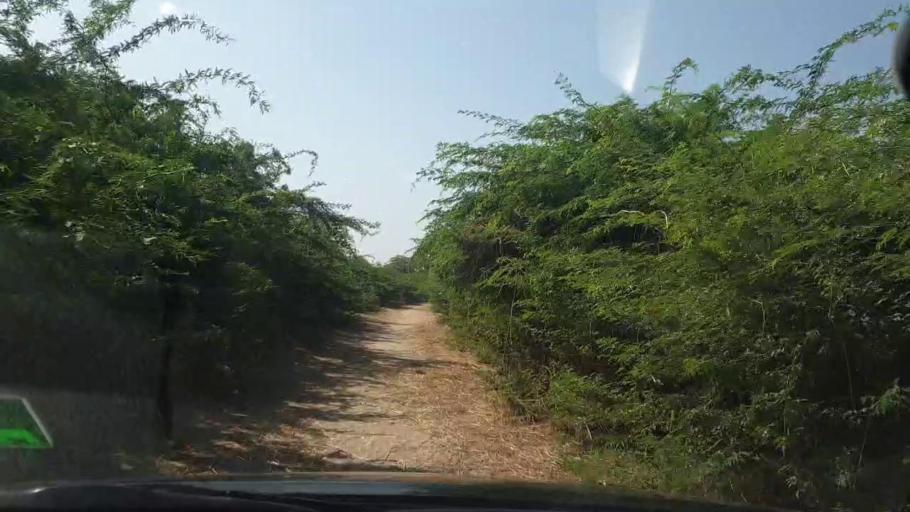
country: PK
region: Sindh
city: Tando Bago
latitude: 24.7708
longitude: 68.9452
